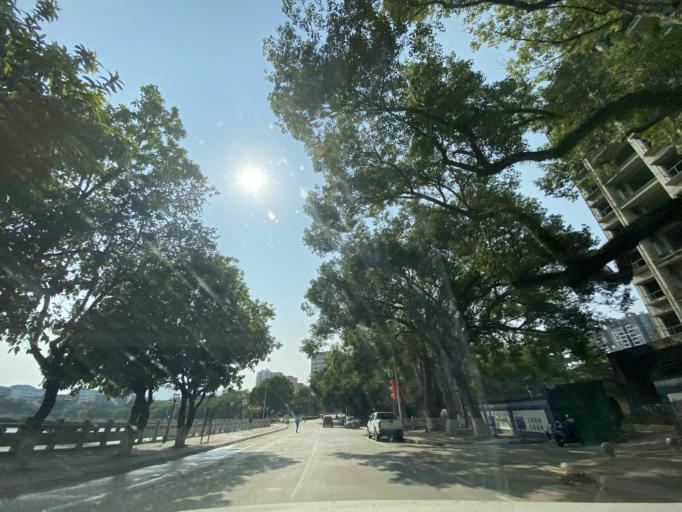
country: CN
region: Hainan
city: Chongshan
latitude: 18.7824
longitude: 109.5124
